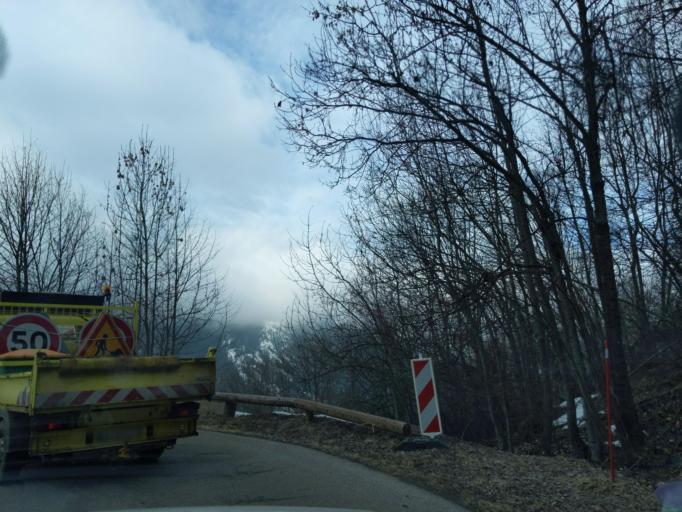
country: FR
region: Rhone-Alpes
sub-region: Departement de la Savoie
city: Belle-Plagne
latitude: 45.5454
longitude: 6.7601
